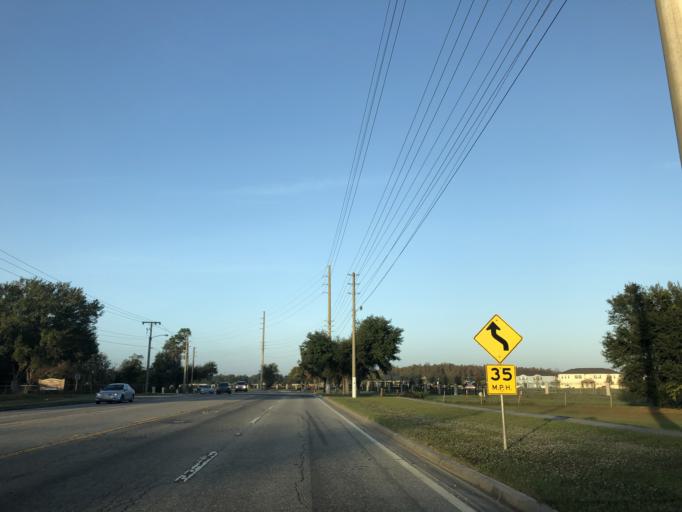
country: US
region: Florida
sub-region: Osceola County
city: Kissimmee
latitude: 28.3264
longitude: -81.4217
